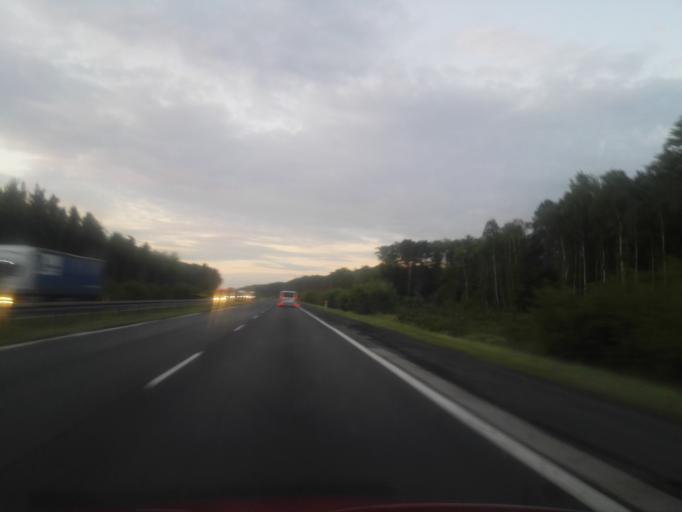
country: PL
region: Lodz Voivodeship
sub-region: Powiat radomszczanski
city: Gomunice
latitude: 51.1595
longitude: 19.4508
